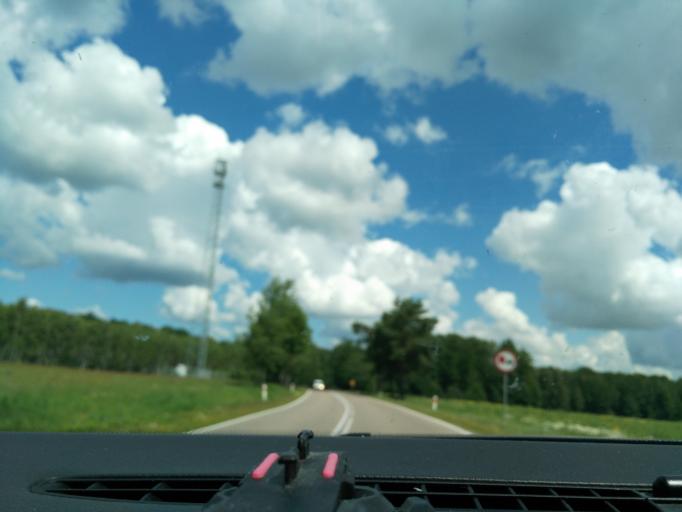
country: PL
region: Podlasie
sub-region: Powiat siemiatycki
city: Dziadkowice
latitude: 52.5309
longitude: 22.9134
